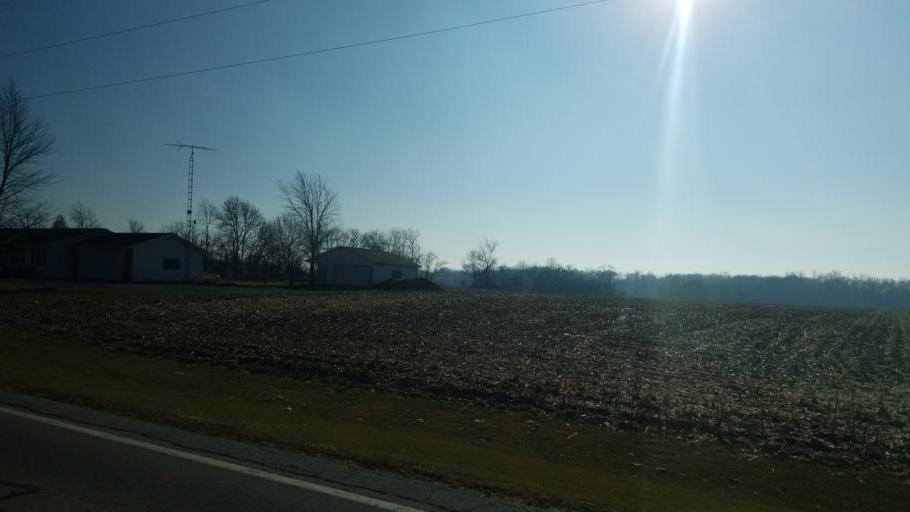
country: US
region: Ohio
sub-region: Seneca County
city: Tiffin
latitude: 41.1244
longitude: -83.1180
